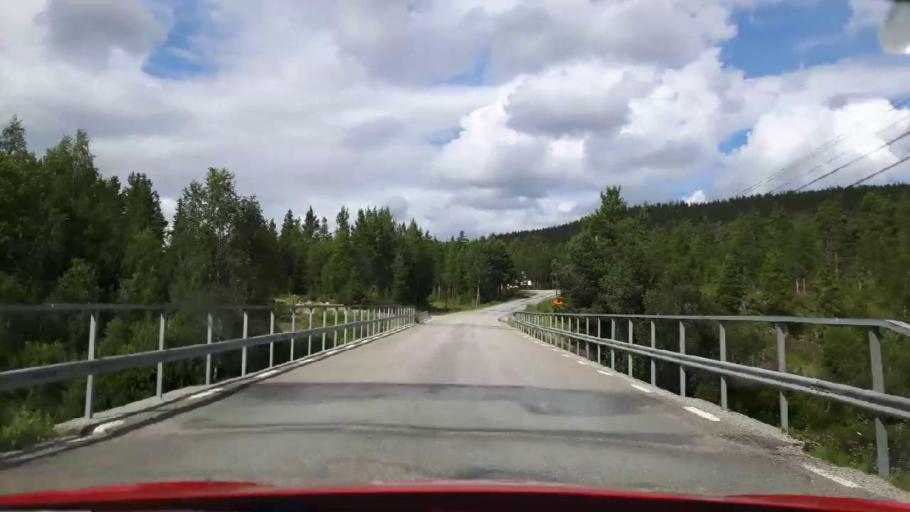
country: NO
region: Hedmark
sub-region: Engerdal
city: Engerdal
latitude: 62.4355
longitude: 12.6784
